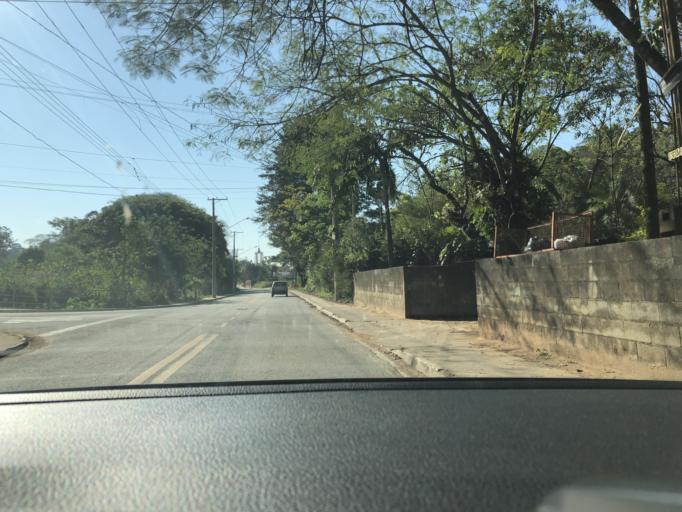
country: BR
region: Sao Paulo
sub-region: Campo Limpo Paulista
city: Campo Limpo Paulista
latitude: -23.1801
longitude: -46.8071
